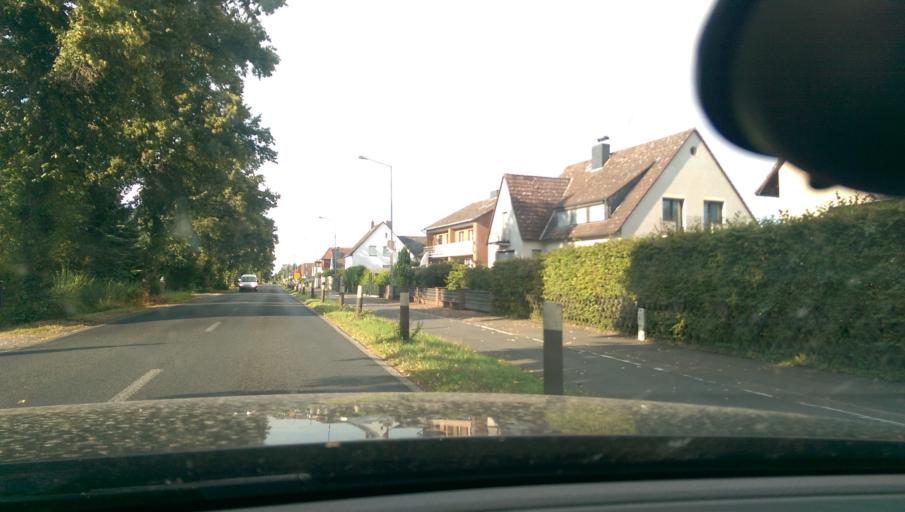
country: DE
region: Lower Saxony
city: Neustadt am Rubenberge
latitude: 52.4825
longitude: 9.4560
